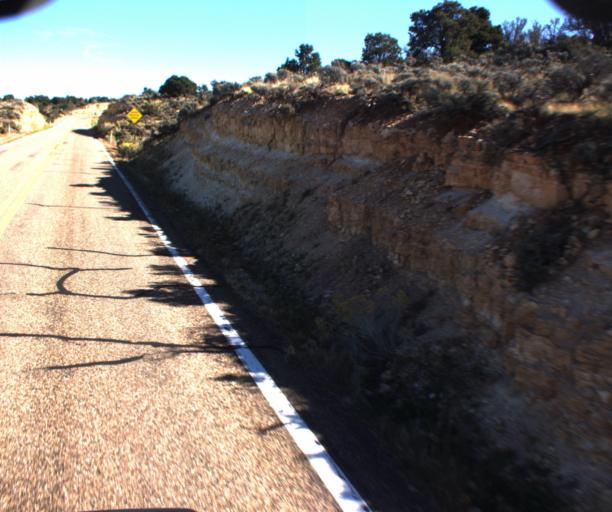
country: US
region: Arizona
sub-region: Coconino County
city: Fredonia
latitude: 36.8469
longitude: -112.2696
